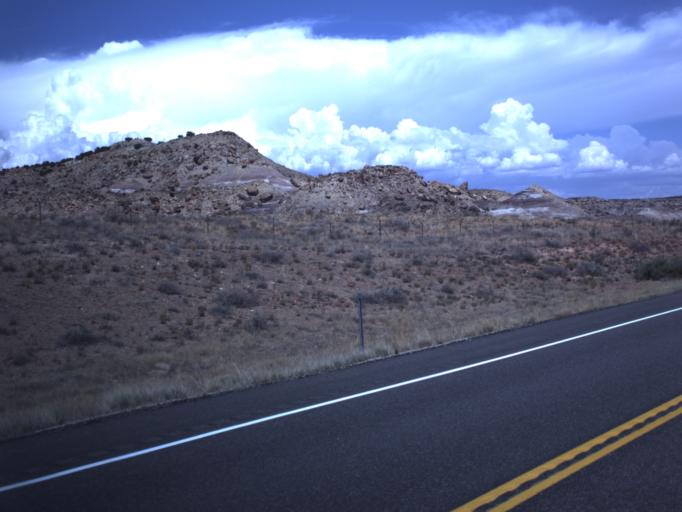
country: US
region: Utah
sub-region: San Juan County
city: Blanding
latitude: 37.4144
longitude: -109.4821
